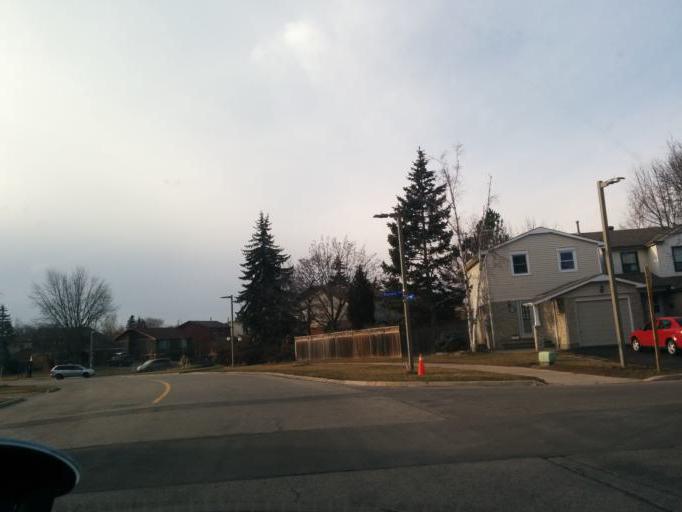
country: CA
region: Ontario
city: Mississauga
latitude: 43.5428
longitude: -79.6945
